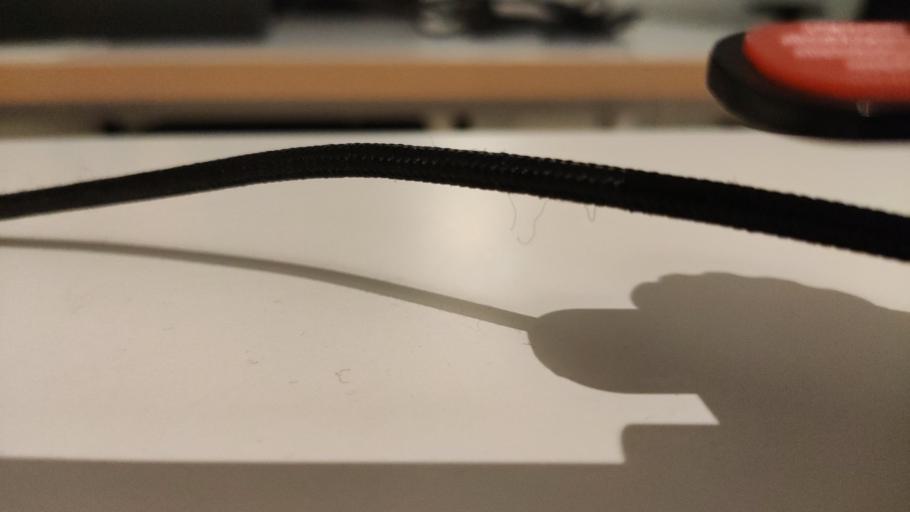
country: RU
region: Moskovskaya
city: Novosin'kovo
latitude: 56.4009
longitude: 37.2556
